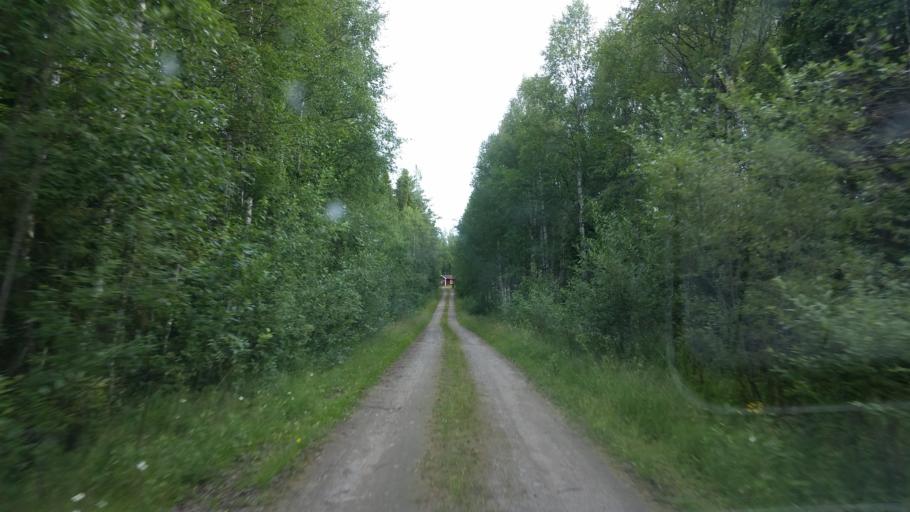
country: SE
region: Vaesternorrland
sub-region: Ange Kommun
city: Ange
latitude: 62.1928
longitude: 15.6470
